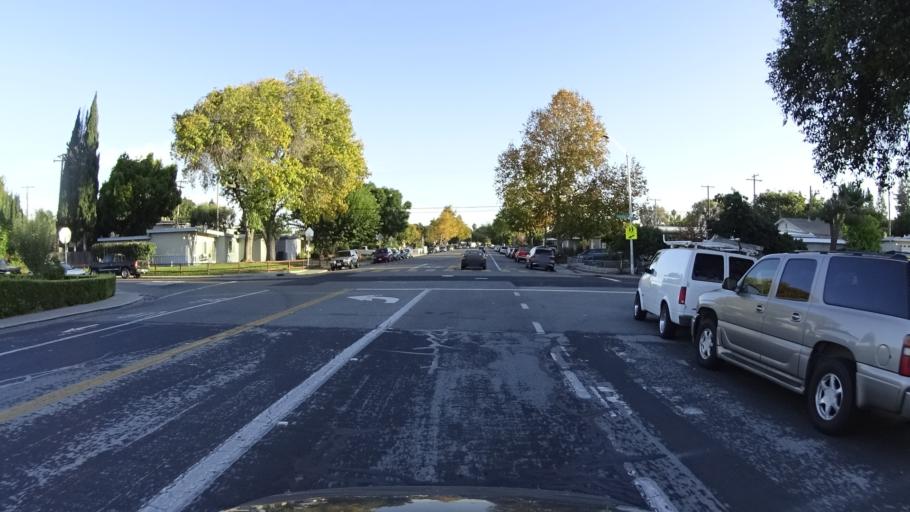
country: US
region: California
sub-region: Santa Clara County
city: Santa Clara
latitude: 37.3598
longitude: -121.9548
